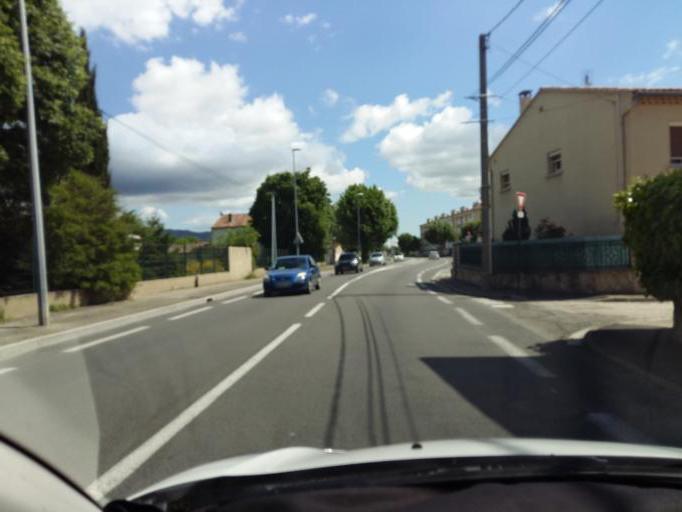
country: FR
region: Provence-Alpes-Cote d'Azur
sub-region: Departement du Vaucluse
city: Cavaillon
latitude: 43.8427
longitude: 5.0454
